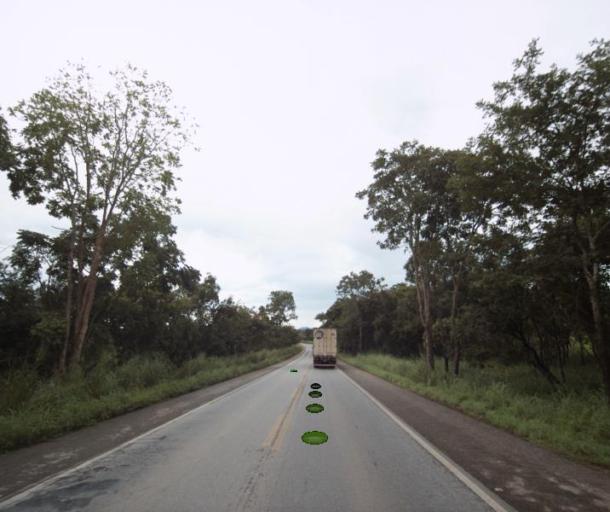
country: BR
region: Goias
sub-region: Porangatu
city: Porangatu
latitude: -13.6480
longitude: -49.0393
